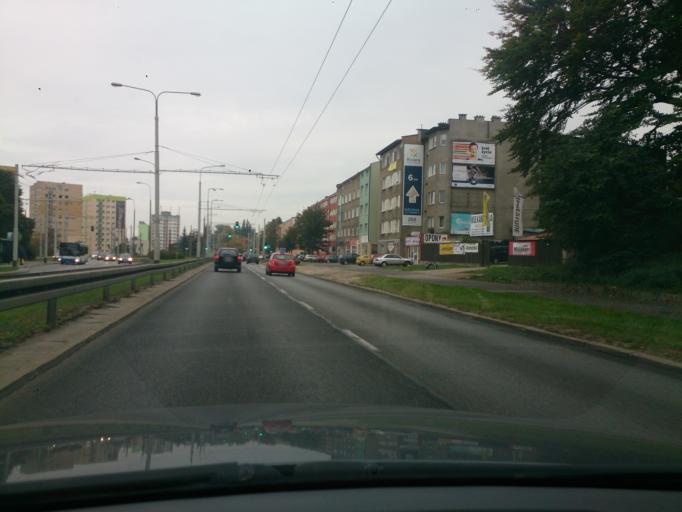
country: PL
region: Pomeranian Voivodeship
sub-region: Gdynia
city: Pogorze
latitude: 54.5366
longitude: 18.4768
